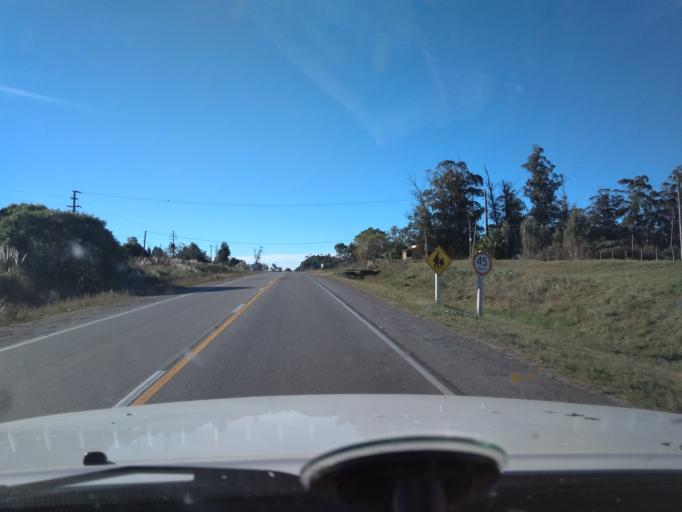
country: UY
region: Canelones
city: Sauce
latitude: -34.6128
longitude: -56.0488
